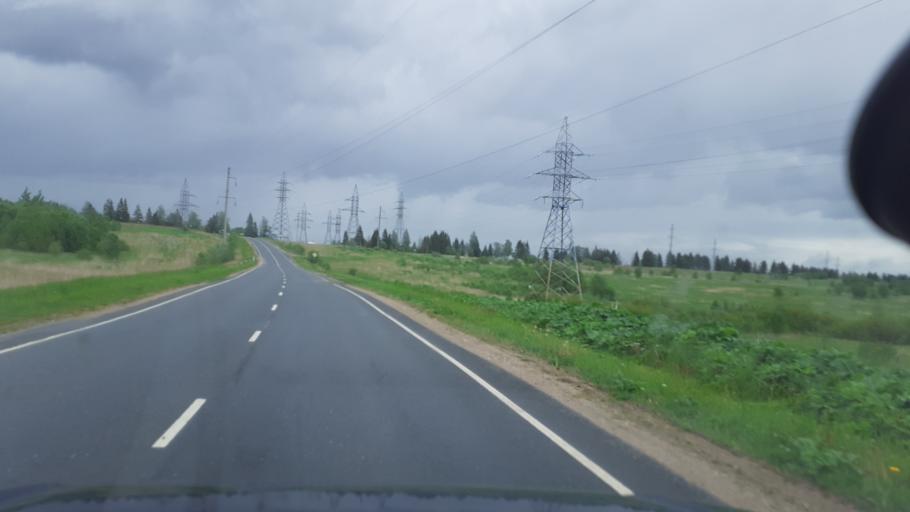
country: RU
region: Moskovskaya
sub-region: Volokolamskiy Rayon
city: Volokolamsk
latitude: 56.0179
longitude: 35.9584
